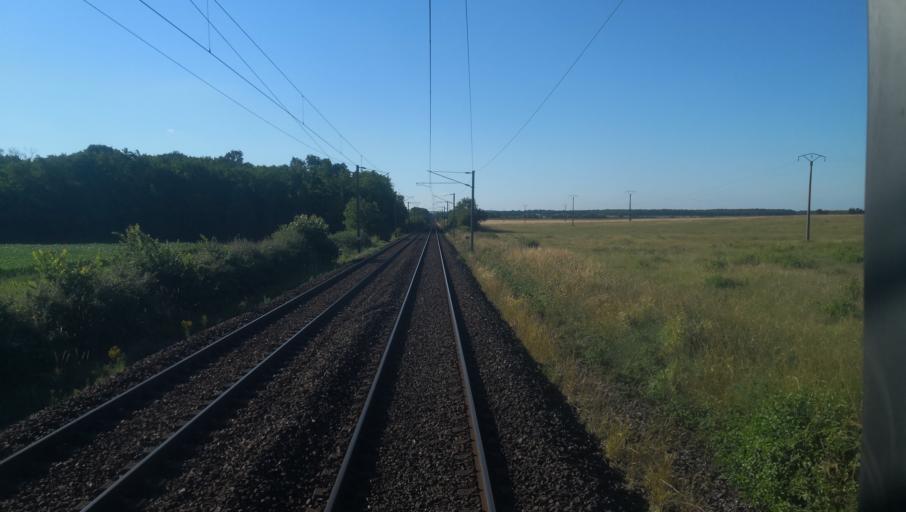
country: FR
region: Bourgogne
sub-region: Departement de la Nievre
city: La Charite-sur-Loire
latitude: 47.2319
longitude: 3.0122
